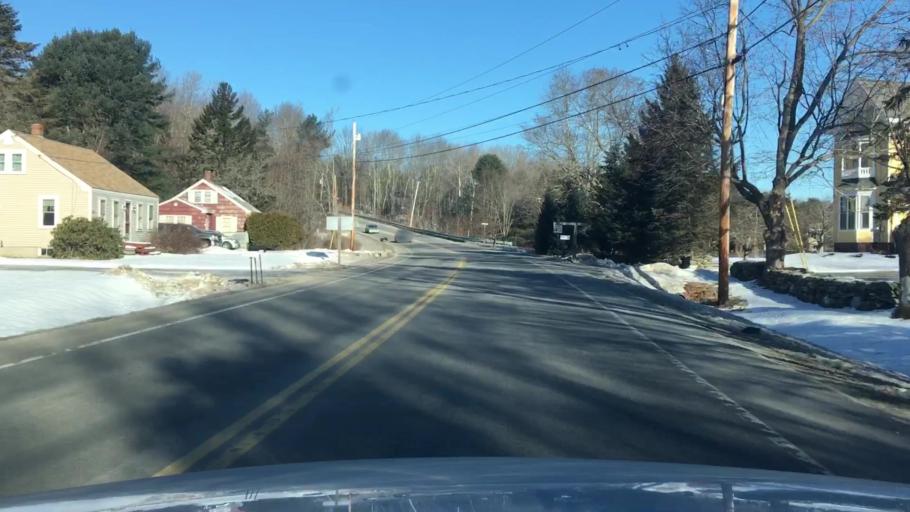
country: US
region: Maine
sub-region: Cumberland County
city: Freeport
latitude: 43.8761
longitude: -70.1070
